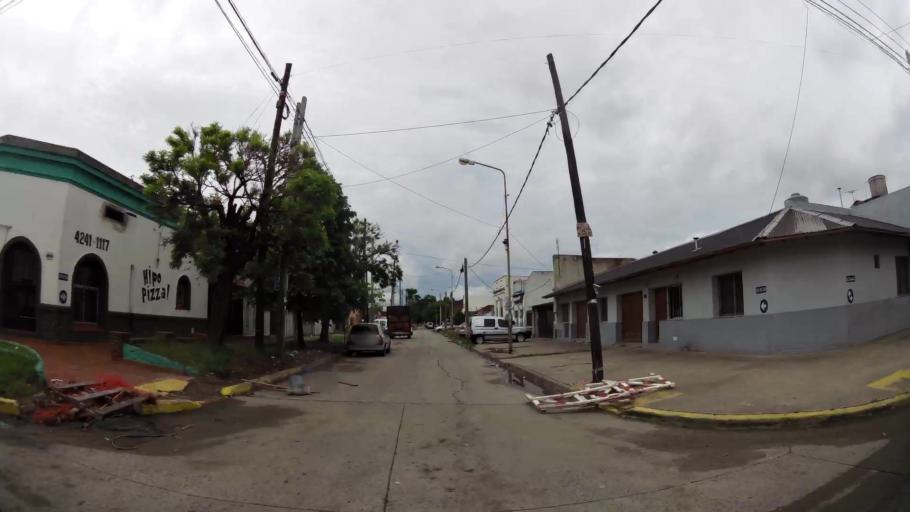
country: AR
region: Buenos Aires
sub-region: Partido de Lanus
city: Lanus
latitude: -34.7289
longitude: -58.3863
